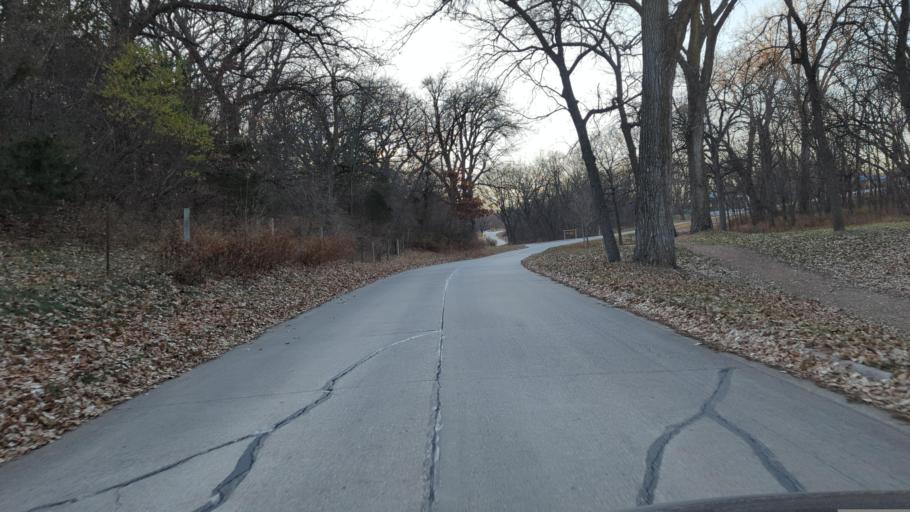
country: US
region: Nebraska
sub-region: Cass County
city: Louisville
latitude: 40.9867
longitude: -96.2205
